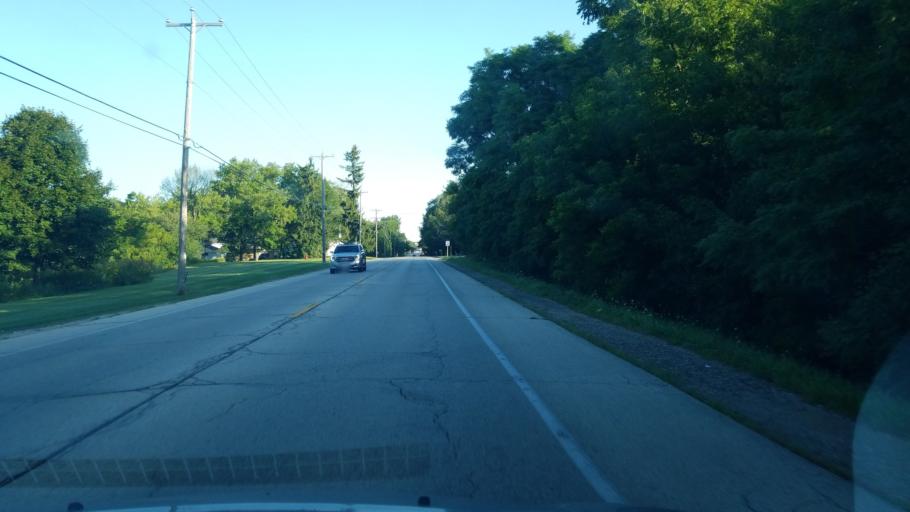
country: US
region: Wisconsin
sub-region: Ozaukee County
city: Thiensville
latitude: 43.2120
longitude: -87.9763
